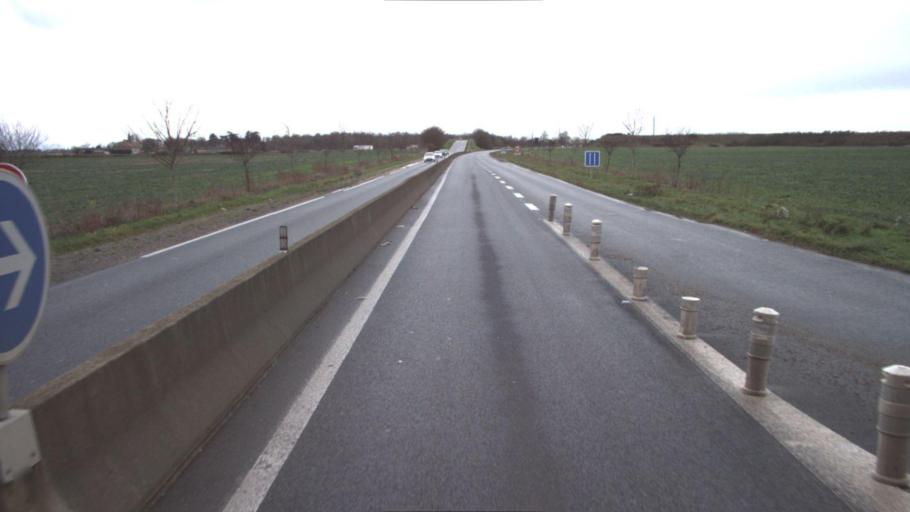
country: FR
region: Ile-de-France
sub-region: Departement de l'Essonne
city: Le Coudray-Montceaux
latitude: 48.5560
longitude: 2.4979
